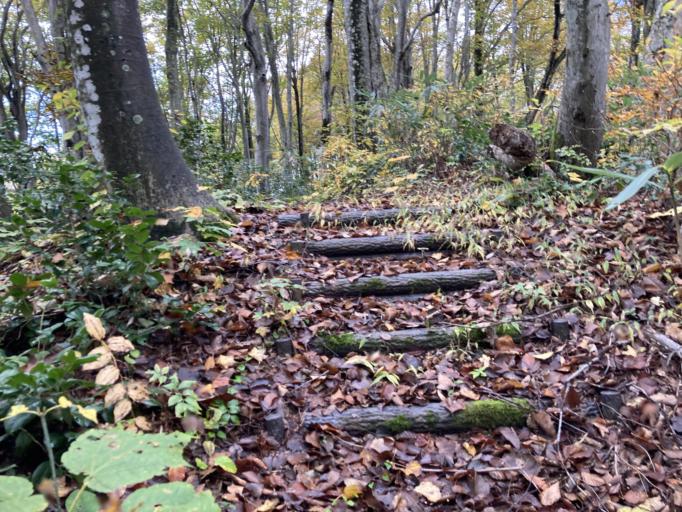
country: JP
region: Niigata
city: Tokamachi
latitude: 37.1548
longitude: 138.6285
